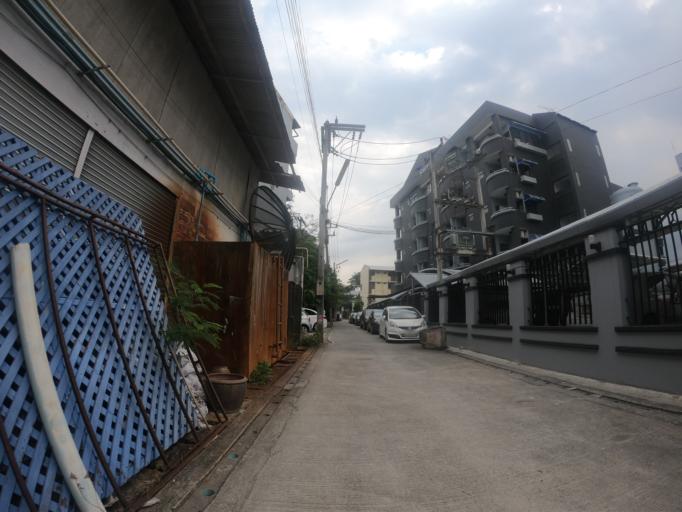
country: TH
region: Chiang Mai
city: Chiang Mai
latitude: 18.8014
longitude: 98.9622
